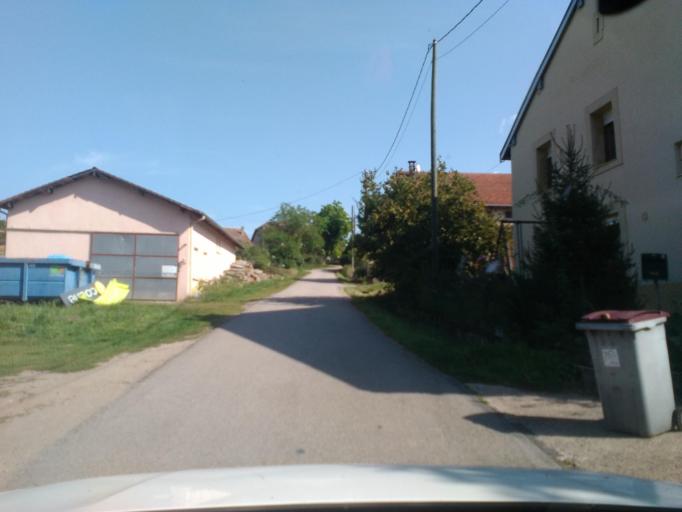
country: FR
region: Lorraine
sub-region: Departement des Vosges
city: Senones
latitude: 48.3541
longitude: 7.0072
